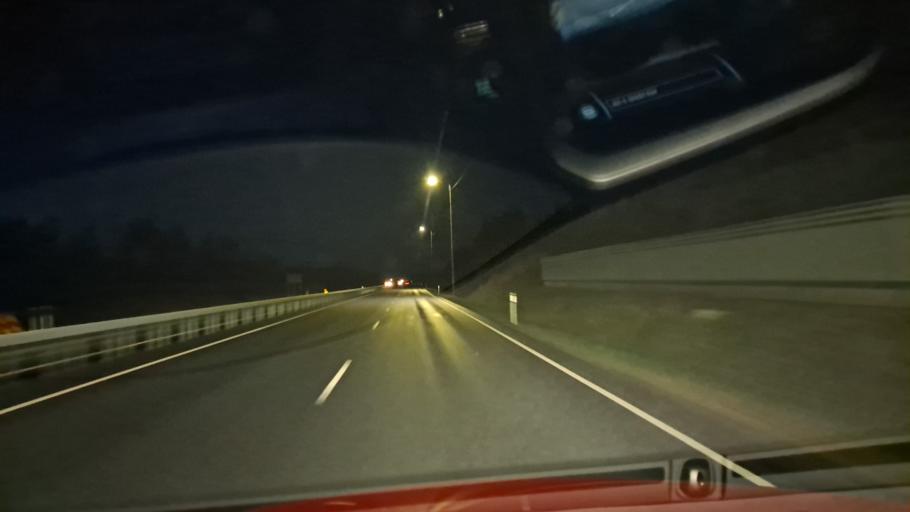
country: FI
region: Northern Ostrobothnia
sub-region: Oulunkaari
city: Kuivaniemi
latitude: 65.5416
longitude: 25.2445
